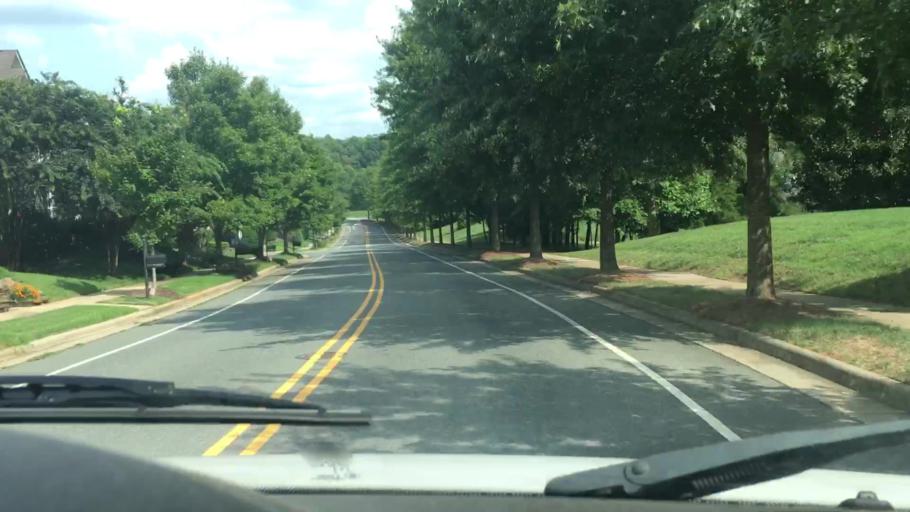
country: US
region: North Carolina
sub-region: Mecklenburg County
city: Huntersville
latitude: 35.4219
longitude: -80.8773
